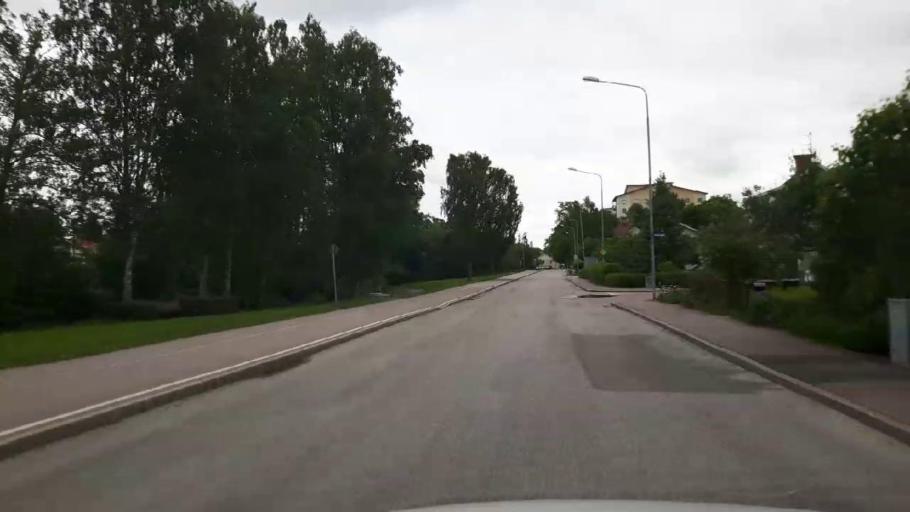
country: SE
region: Vaestmanland
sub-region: Kopings Kommun
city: Koping
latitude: 59.5179
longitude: 15.9848
